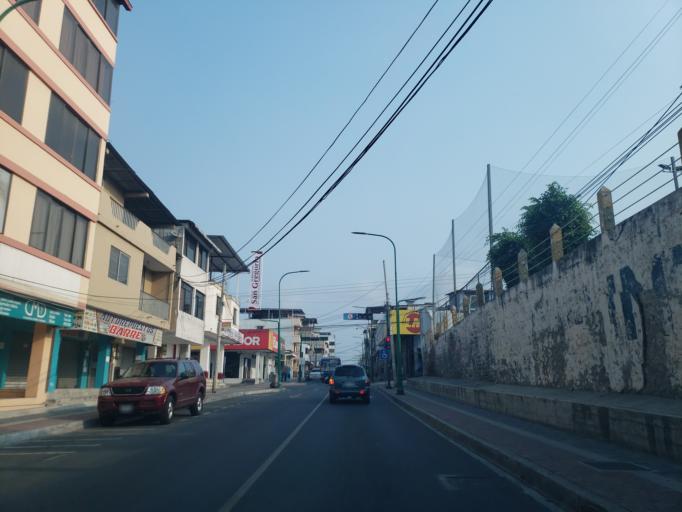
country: EC
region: Manabi
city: Manta
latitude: -0.9514
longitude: -80.7299
